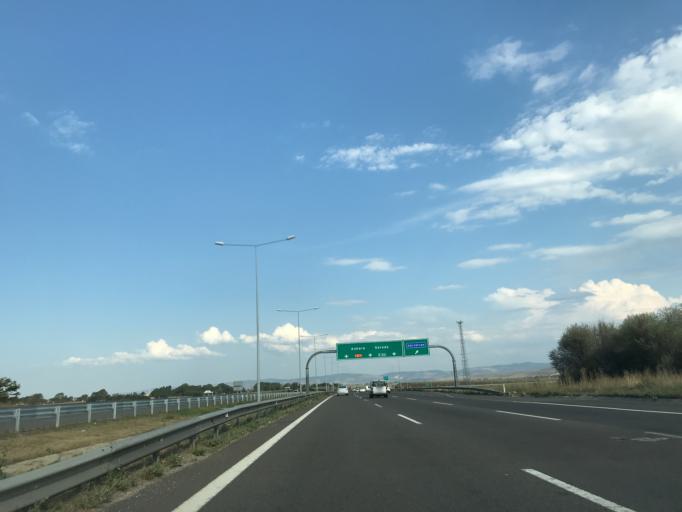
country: TR
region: Bolu
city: Dortdivan
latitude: 40.7454
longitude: 32.1106
